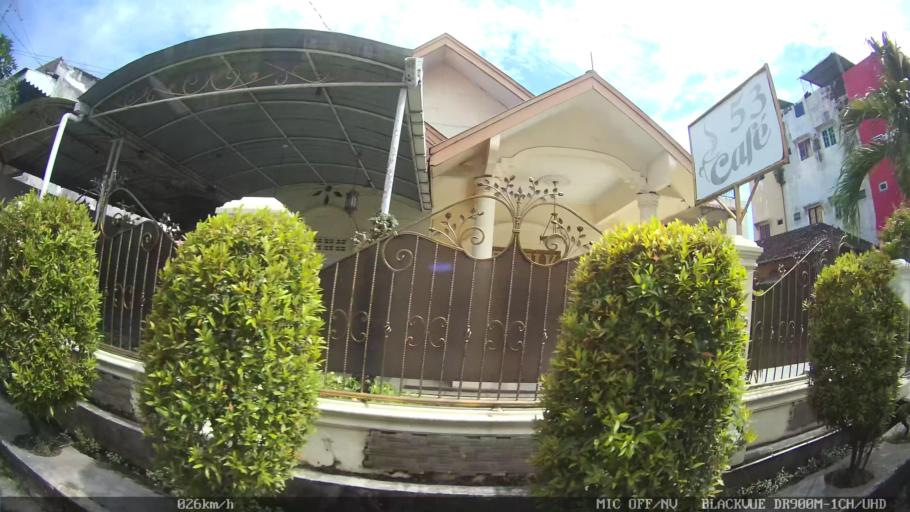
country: ID
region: North Sumatra
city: Medan
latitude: 3.5875
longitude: 98.7106
